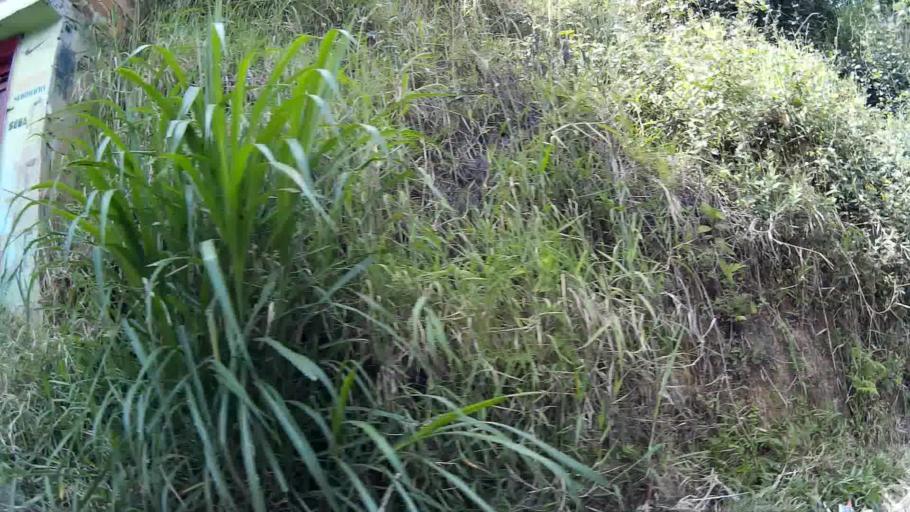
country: CO
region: Antioquia
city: Medellin
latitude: 6.2698
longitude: -75.6280
